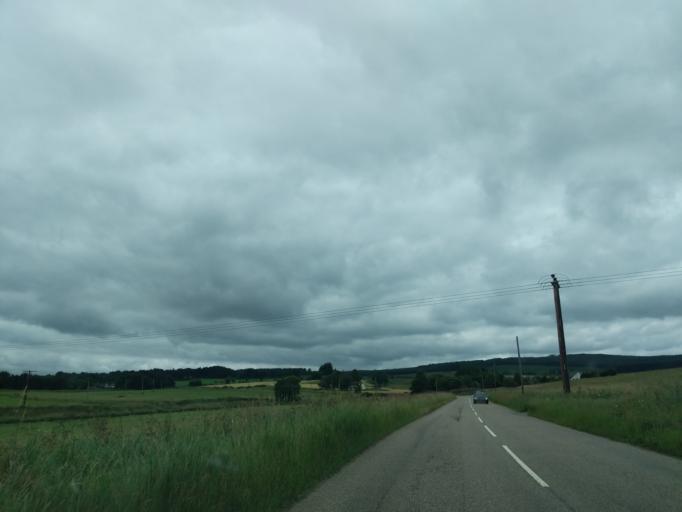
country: GB
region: Scotland
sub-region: Moray
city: Rothes
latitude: 57.4901
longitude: -3.2312
